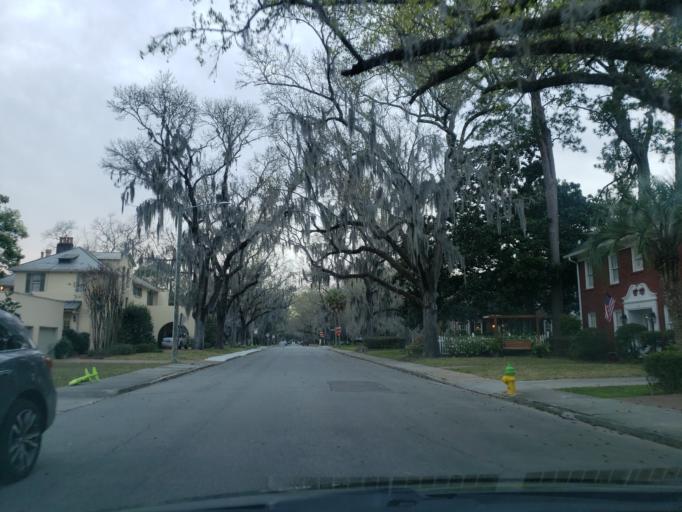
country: US
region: Georgia
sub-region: Chatham County
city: Savannah
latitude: 32.0480
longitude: -81.0910
